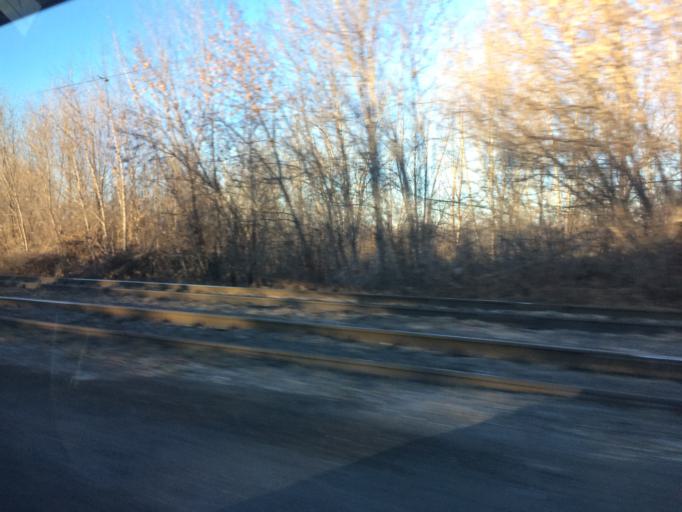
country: RU
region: Chelyabinsk
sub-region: Gorod Magnitogorsk
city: Magnitogorsk
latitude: 53.4074
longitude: 59.0301
